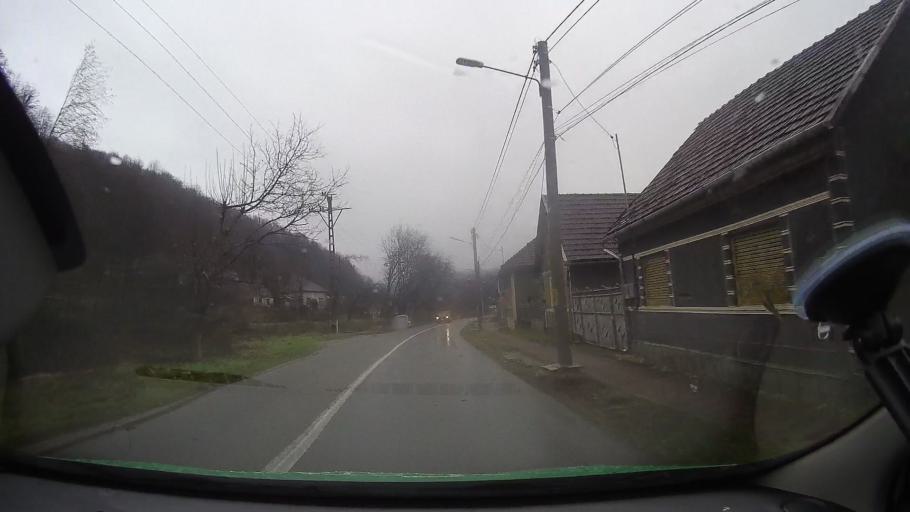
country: RO
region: Arad
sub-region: Comuna Moneasa
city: Moneasa
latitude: 46.4499
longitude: 22.2472
